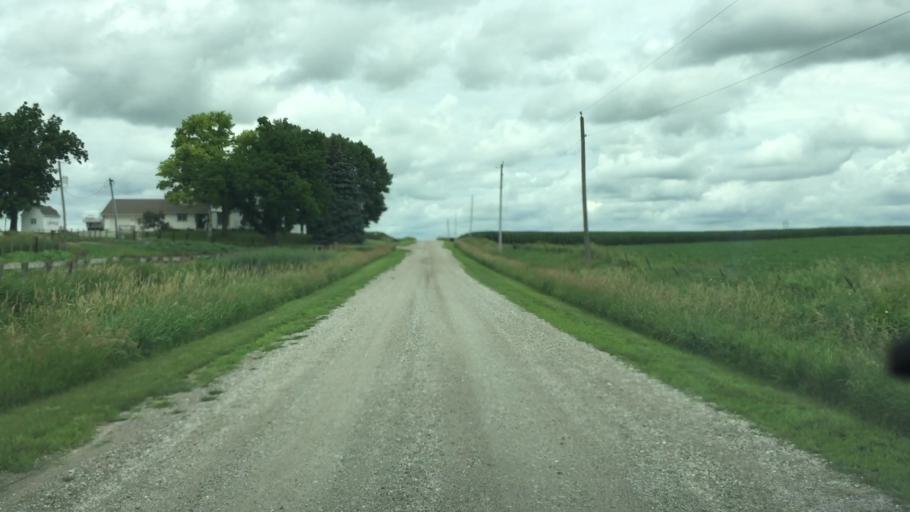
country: US
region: Iowa
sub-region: Jasper County
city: Monroe
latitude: 41.5684
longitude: -93.1208
